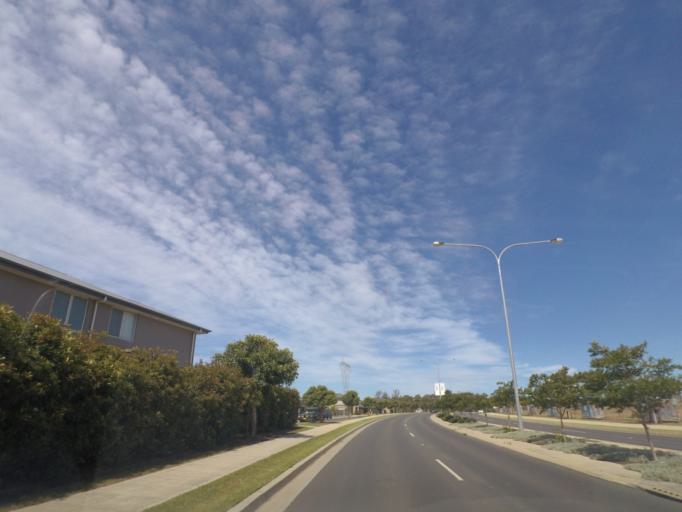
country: AU
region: New South Wales
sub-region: Camden
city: Narellan Vale
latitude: -34.0245
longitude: 150.7807
